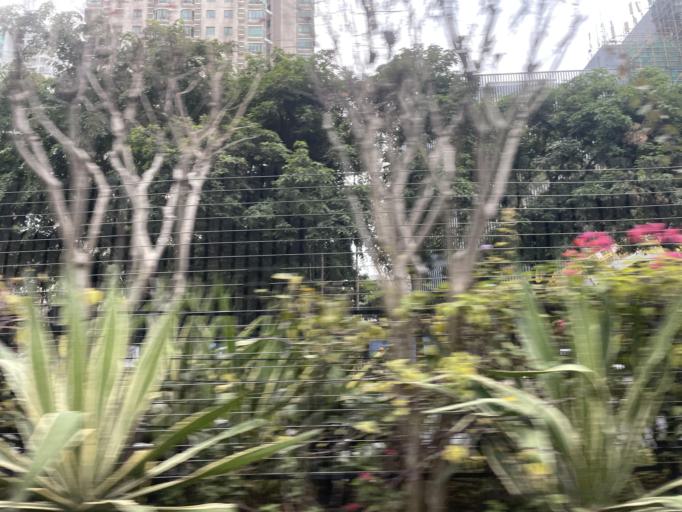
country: CN
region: Guangdong
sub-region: Shenzhen
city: Shenzhen
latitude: 22.5206
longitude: 114.0430
